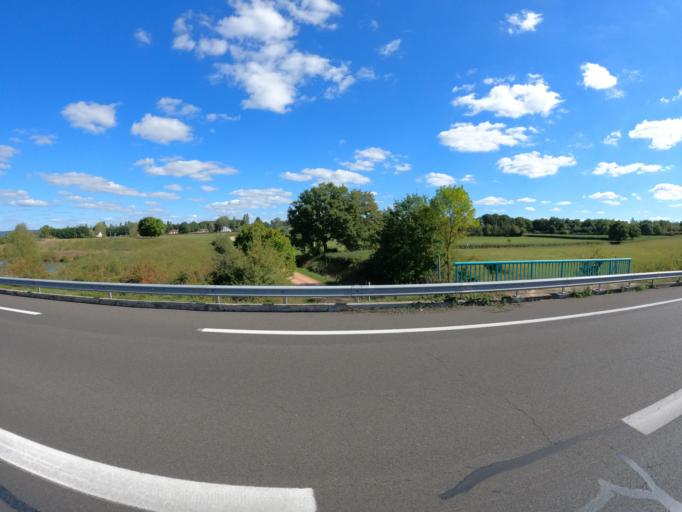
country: FR
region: Auvergne
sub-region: Departement de l'Allier
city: Domerat
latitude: 46.3572
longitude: 2.5482
